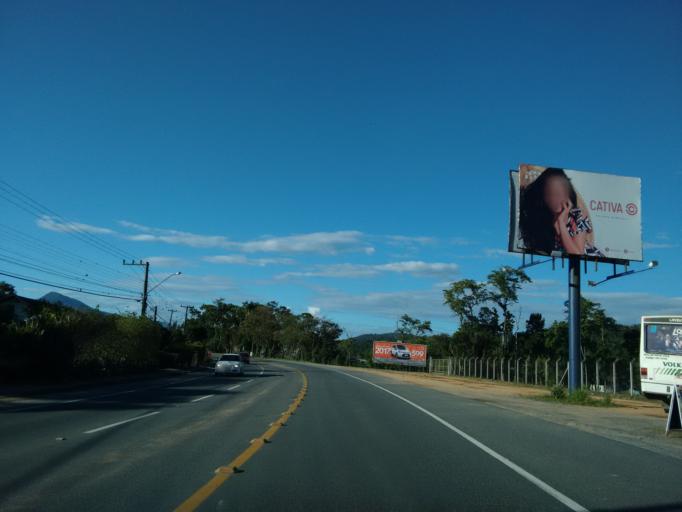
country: BR
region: Santa Catarina
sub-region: Pomerode
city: Pomerode
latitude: -26.7645
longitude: -49.1693
